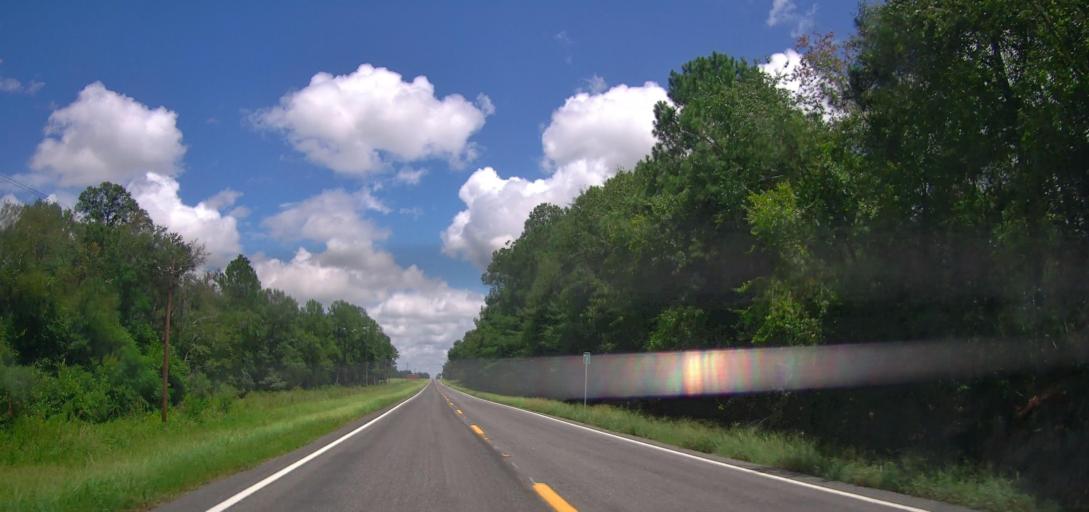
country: US
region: Georgia
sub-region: Turner County
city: Ashburn
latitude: 31.7888
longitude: -83.5947
